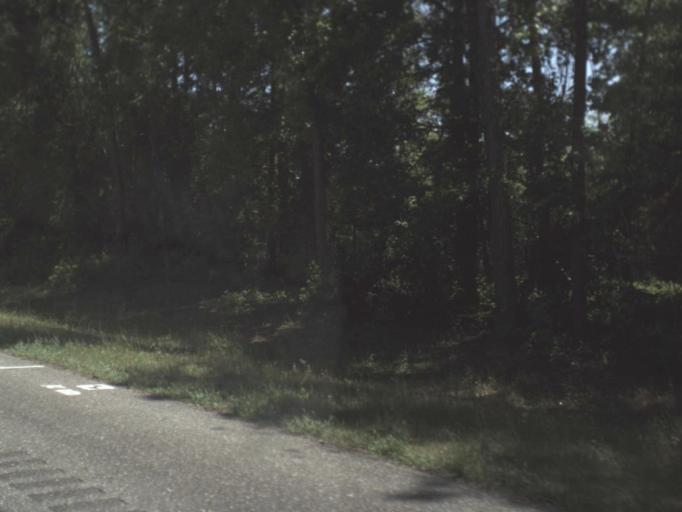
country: US
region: Florida
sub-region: Jefferson County
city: Monticello
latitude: 30.4578
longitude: -83.7712
